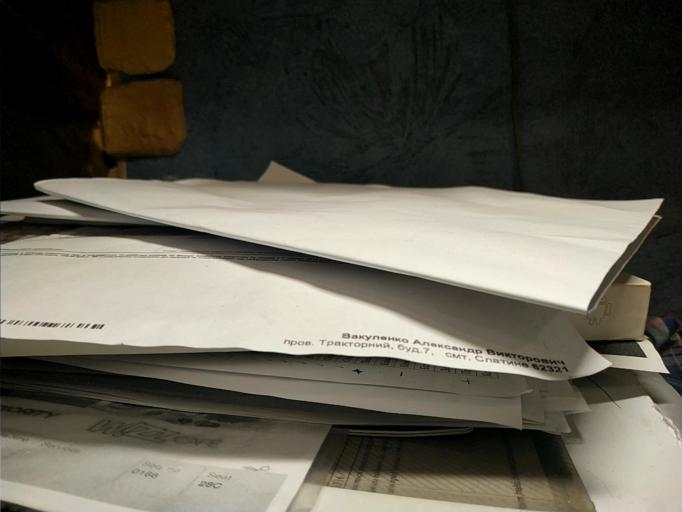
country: RU
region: Tverskaya
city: Zubtsov
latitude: 56.1009
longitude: 34.6838
